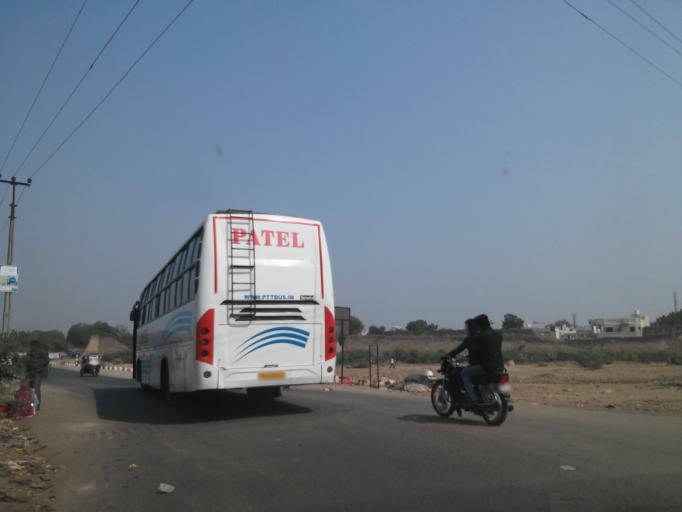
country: IN
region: Gujarat
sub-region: Kachchh
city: Mundra
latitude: 22.8400
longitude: 69.7181
